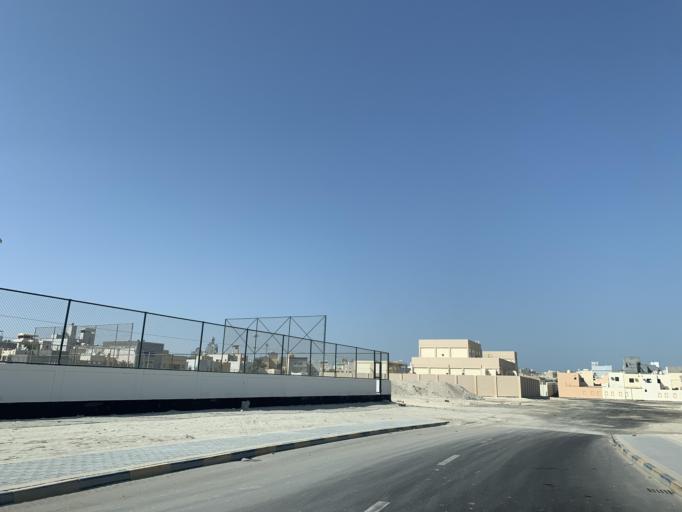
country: BH
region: Central Governorate
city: Madinat Hamad
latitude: 26.1262
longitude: 50.4830
